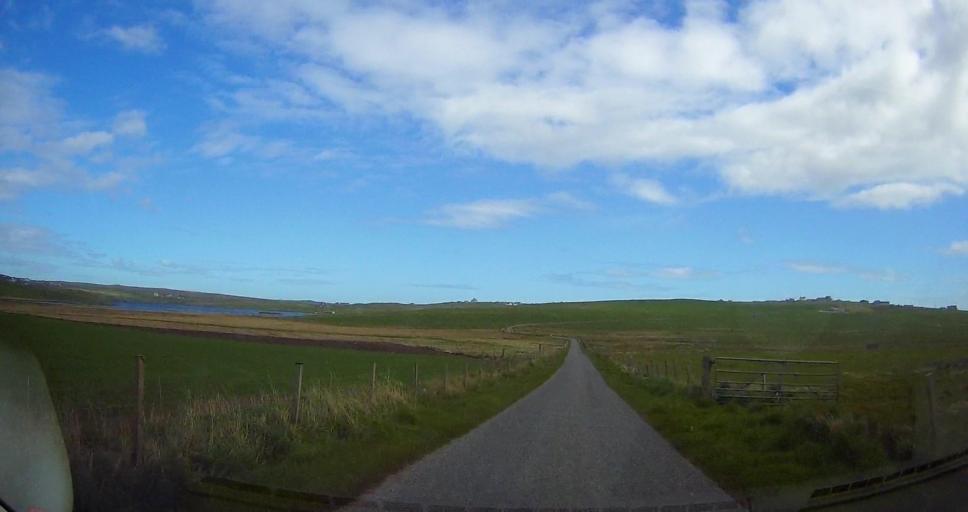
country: GB
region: Scotland
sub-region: Shetland Islands
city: Sandwick
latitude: 59.9230
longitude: -1.3301
